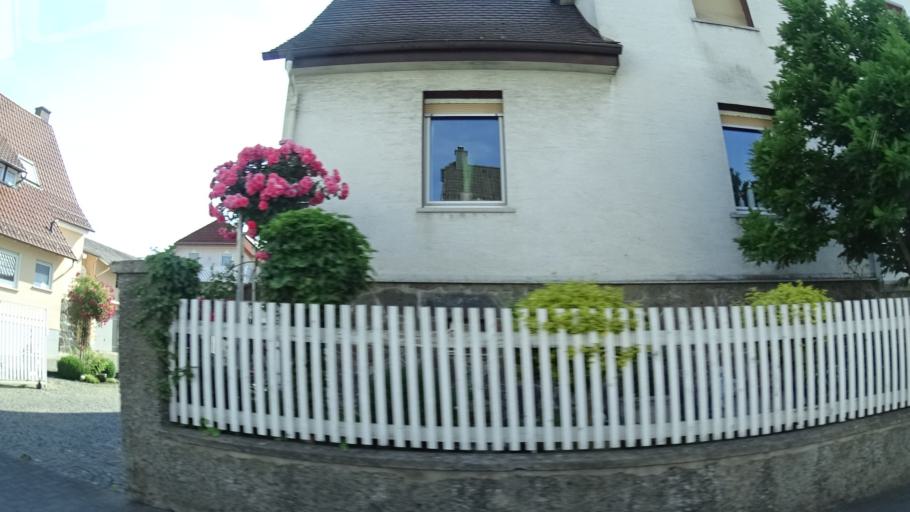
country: DE
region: Hesse
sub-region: Regierungsbezirk Giessen
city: Rabenau
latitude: 50.6748
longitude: 8.8234
